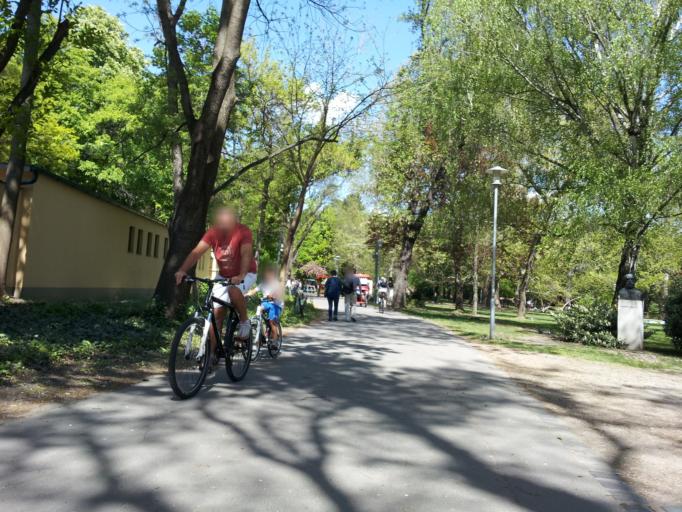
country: HU
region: Budapest
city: Budapest III. keruelet
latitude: 47.5296
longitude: 19.0506
